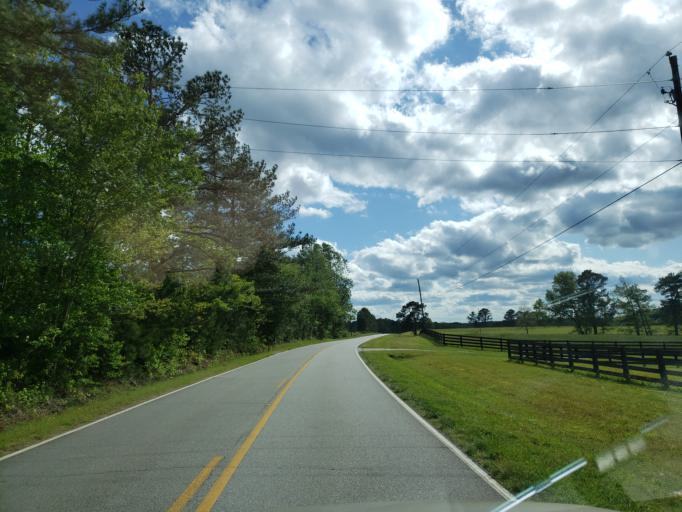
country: US
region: Georgia
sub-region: Carroll County
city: Mount Zion
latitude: 33.6728
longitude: -85.1911
